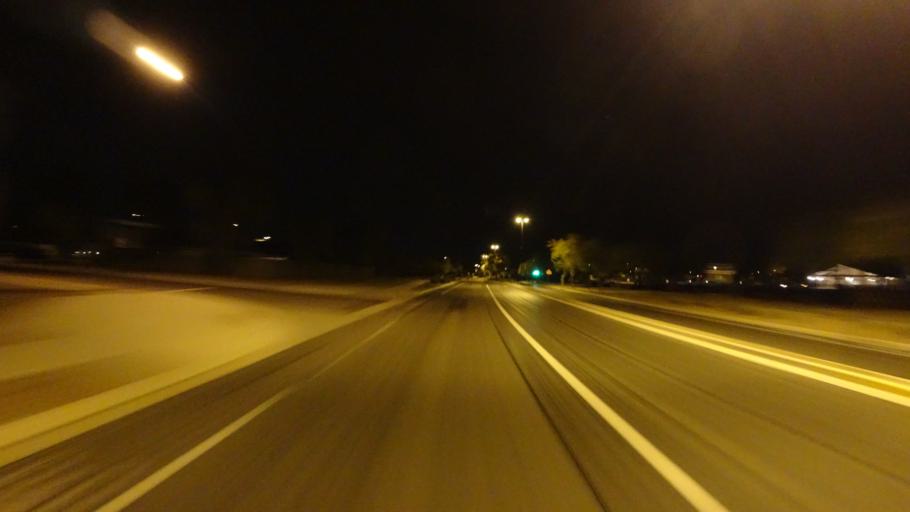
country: US
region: Arizona
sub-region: Maricopa County
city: Queen Creek
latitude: 33.2868
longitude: -111.6979
